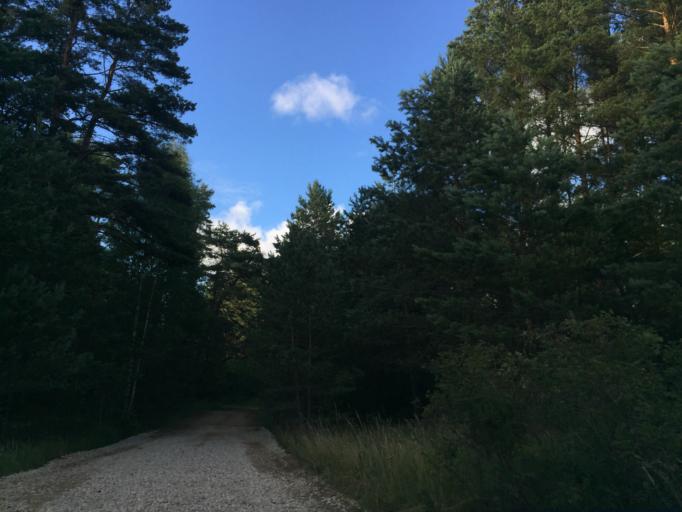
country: LV
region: Adazi
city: Adazi
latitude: 57.1322
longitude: 24.3459
